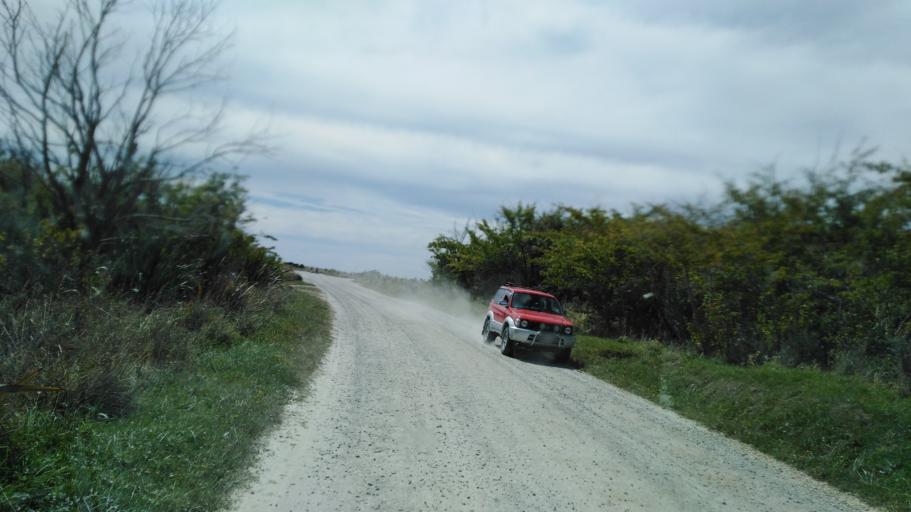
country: NZ
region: West Coast
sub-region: Buller District
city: Westport
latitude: -41.7357
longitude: 171.6054
